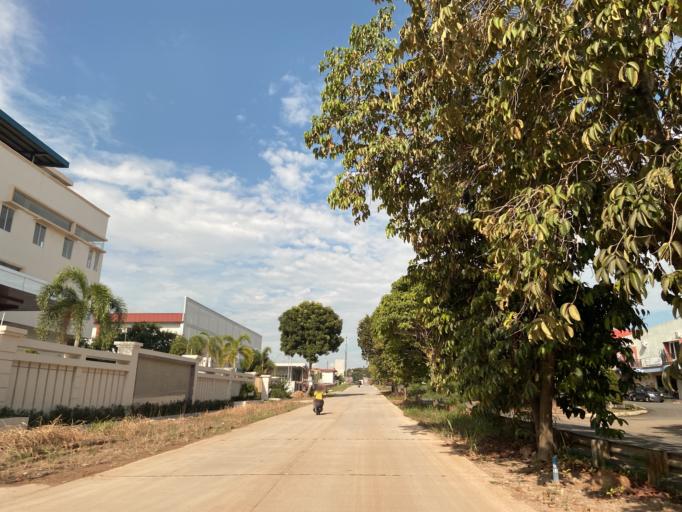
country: SG
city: Singapore
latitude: 1.1118
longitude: 104.0720
